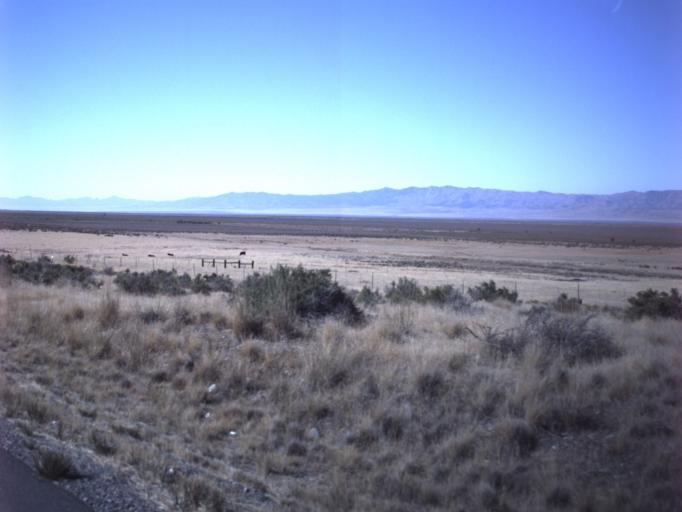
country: US
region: Utah
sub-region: Tooele County
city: Grantsville
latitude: 40.6694
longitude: -112.6744
